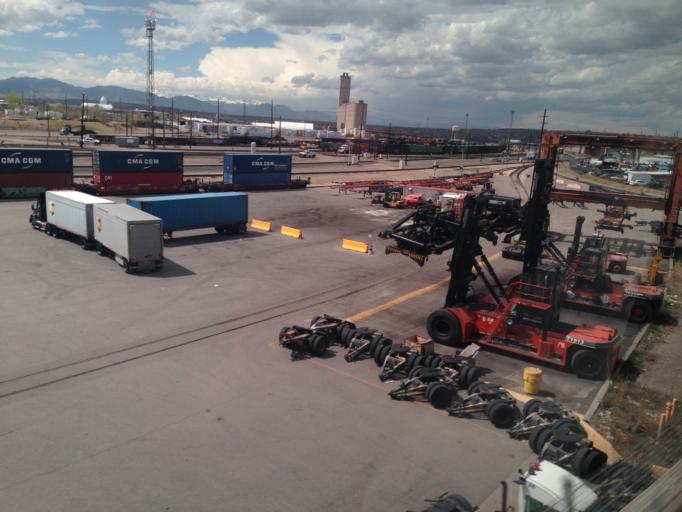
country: US
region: Colorado
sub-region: Adams County
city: Twin Lakes
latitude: 39.7974
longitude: -104.9967
